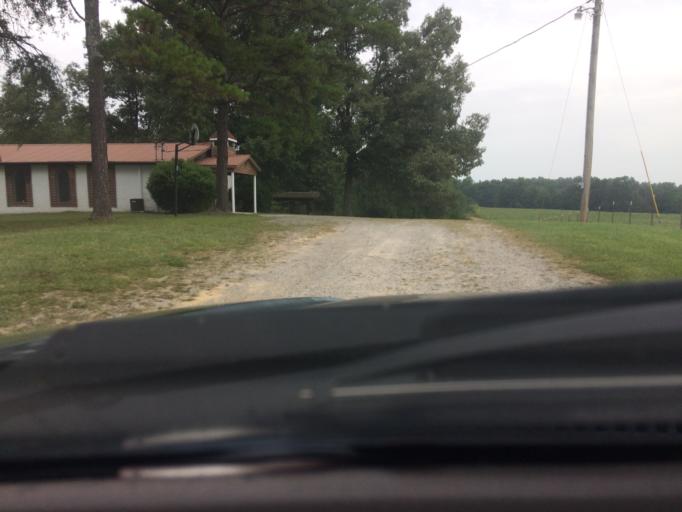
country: US
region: Tennessee
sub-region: Fentress County
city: Grimsley
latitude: 36.1798
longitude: -84.8988
